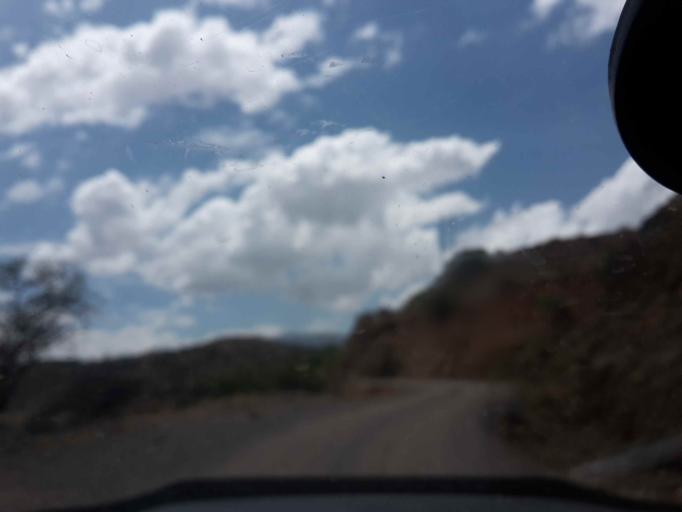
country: BO
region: Cochabamba
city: Sipe Sipe
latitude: -17.5481
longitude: -66.4803
